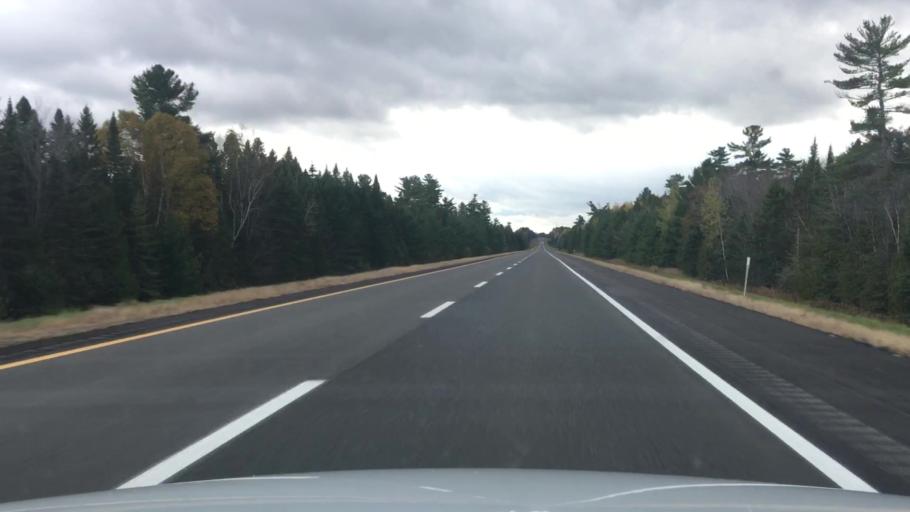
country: US
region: Maine
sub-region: Penobscot County
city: Patten
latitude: 46.0747
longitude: -68.2200
